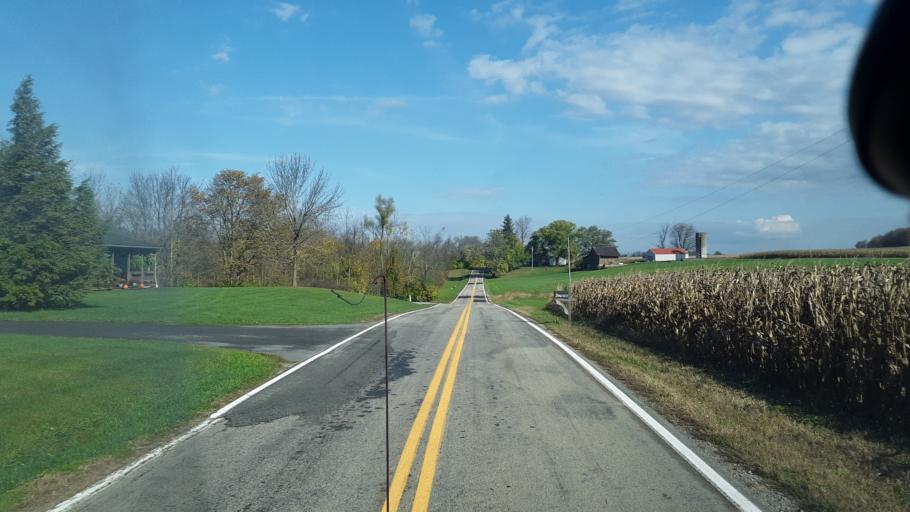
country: US
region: Ohio
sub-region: Highland County
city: Leesburg
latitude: 39.3264
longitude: -83.5858
